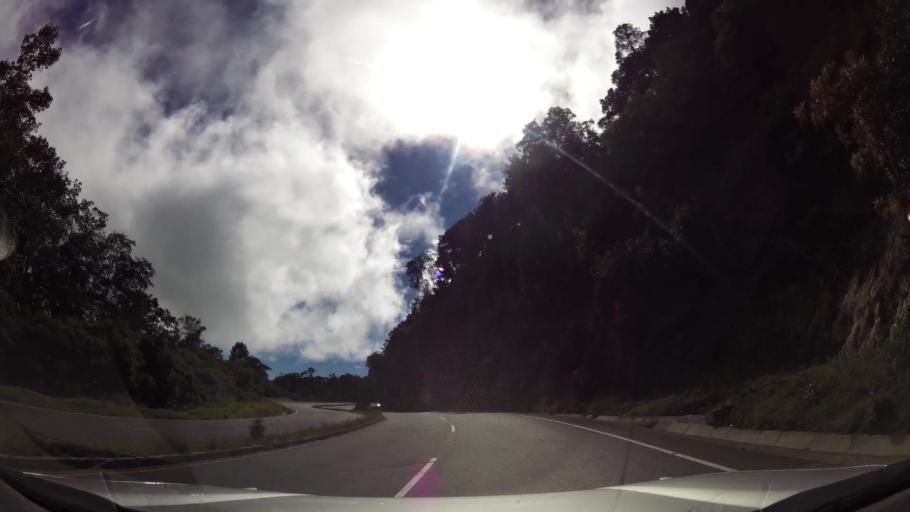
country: GT
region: Solola
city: Santa Catarina Ixtahuacan
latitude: 14.8436
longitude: -91.3779
